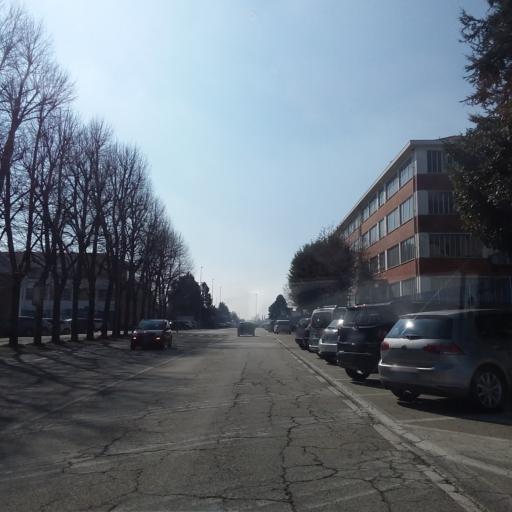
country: IT
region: Piedmont
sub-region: Provincia di Torino
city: Tetti Neirotti
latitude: 45.0662
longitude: 7.5510
